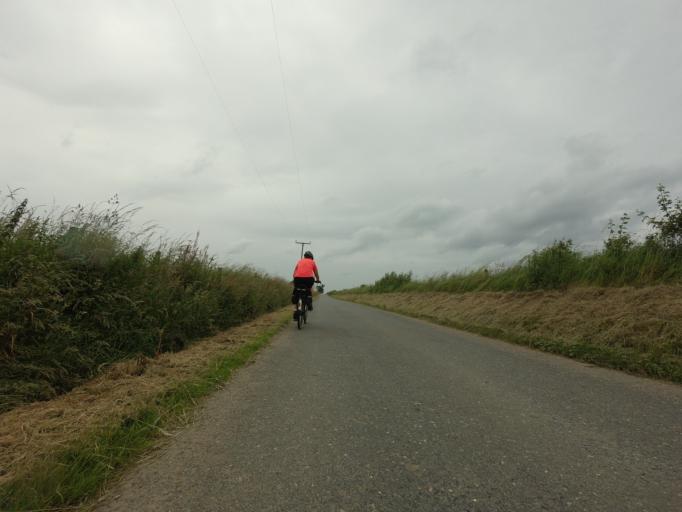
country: GB
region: Scotland
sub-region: Aberdeenshire
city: Portsoy
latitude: 57.6625
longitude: -2.7500
